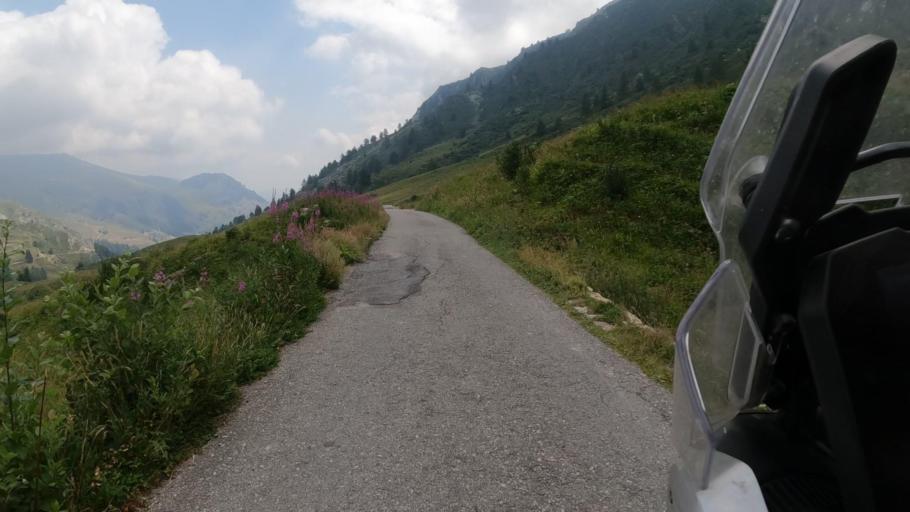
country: IT
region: Piedmont
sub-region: Provincia di Cuneo
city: Campomolino
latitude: 44.3905
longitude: 7.1496
